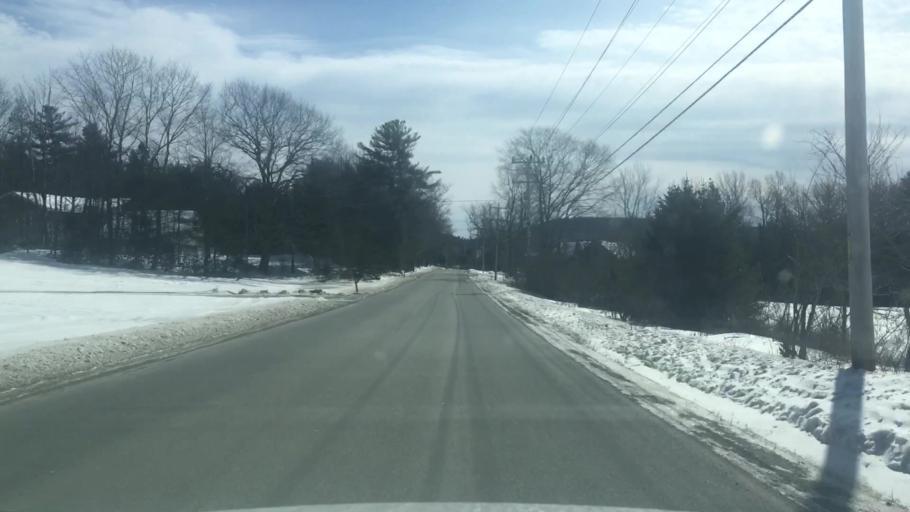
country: US
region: Maine
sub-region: Penobscot County
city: Holden
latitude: 44.7437
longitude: -68.6302
